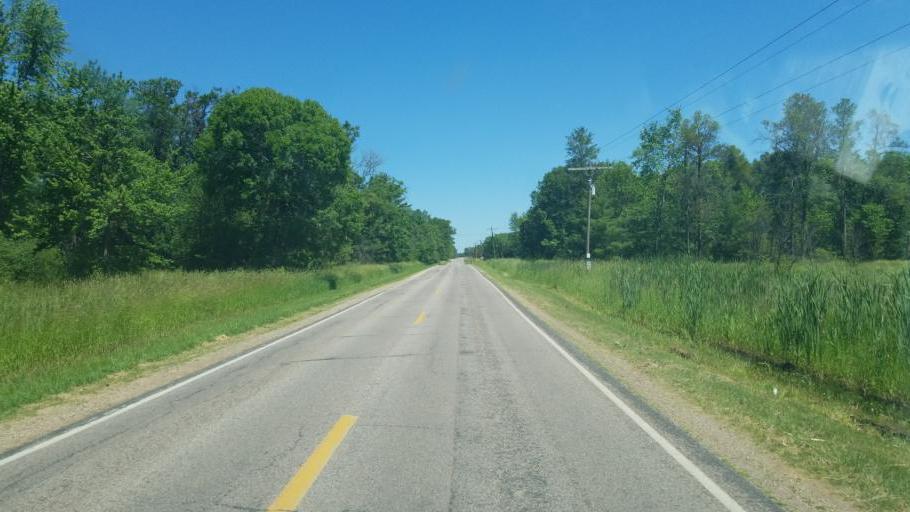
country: US
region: Wisconsin
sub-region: Adams County
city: Adams
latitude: 43.9485
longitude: -89.9377
